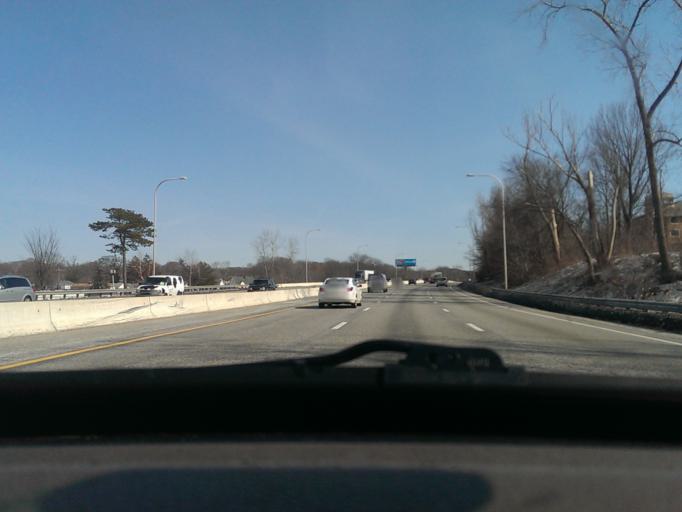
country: US
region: Massachusetts
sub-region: Bristol County
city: Seekonk
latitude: 41.8093
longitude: -71.3453
